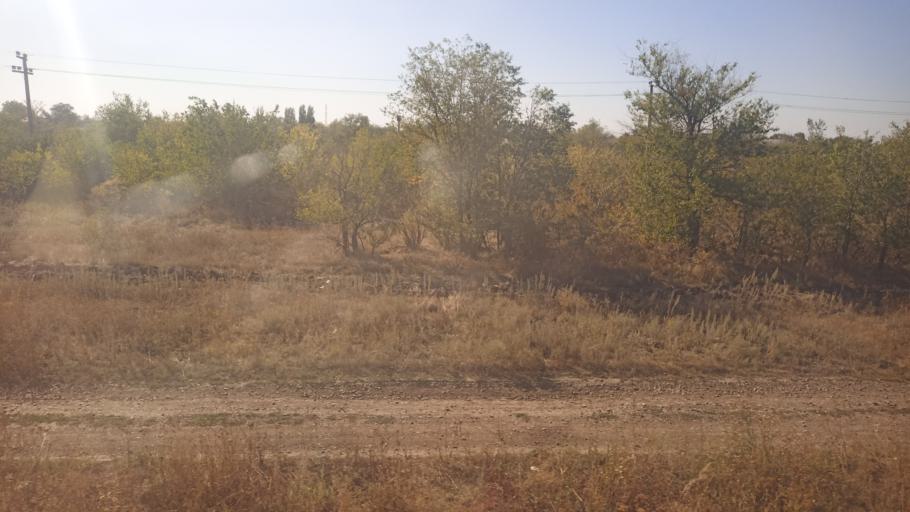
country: RU
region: Saratov
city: Pushkino
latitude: 51.2304
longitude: 46.9854
